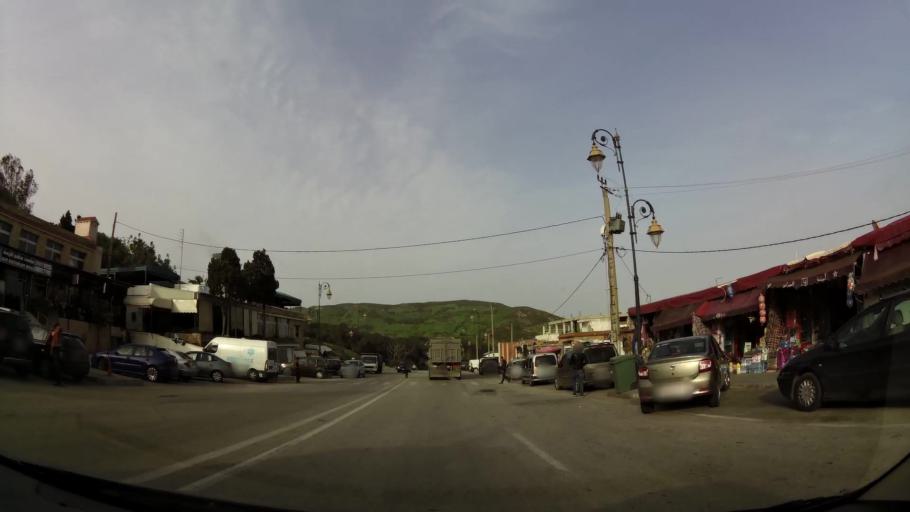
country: MA
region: Tanger-Tetouan
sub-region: Tetouan
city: Saddina
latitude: 35.5478
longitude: -5.5552
